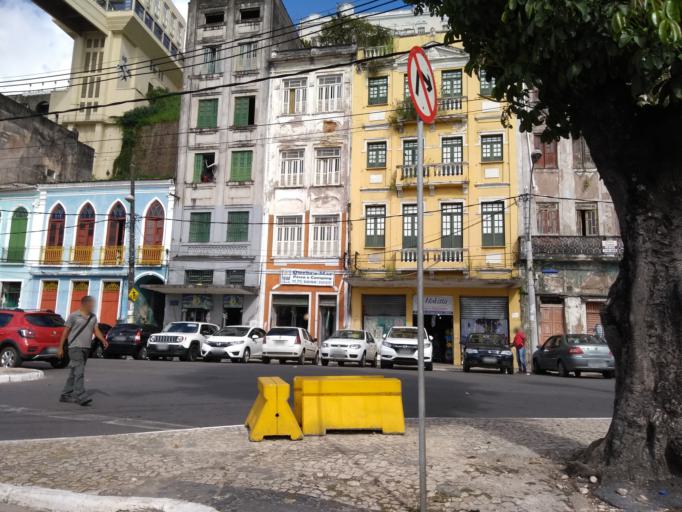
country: BR
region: Bahia
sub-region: Salvador
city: Salvador
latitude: -12.9744
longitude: -38.5140
